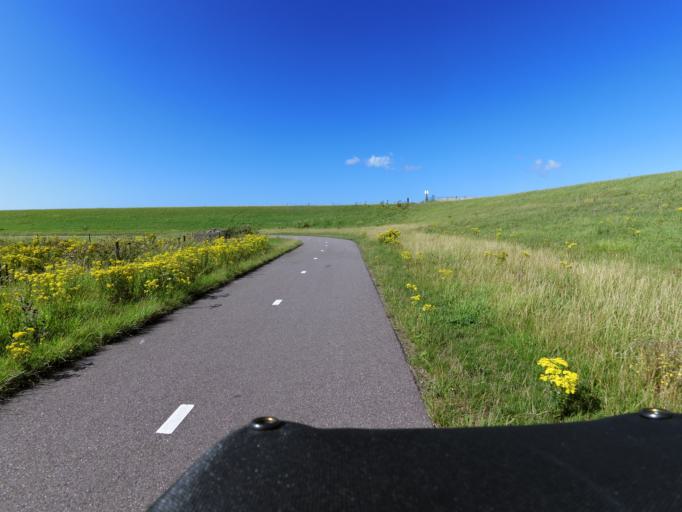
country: NL
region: South Holland
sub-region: Gemeente Goeree-Overflakkee
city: Goedereede
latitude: 51.7833
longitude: 4.0385
